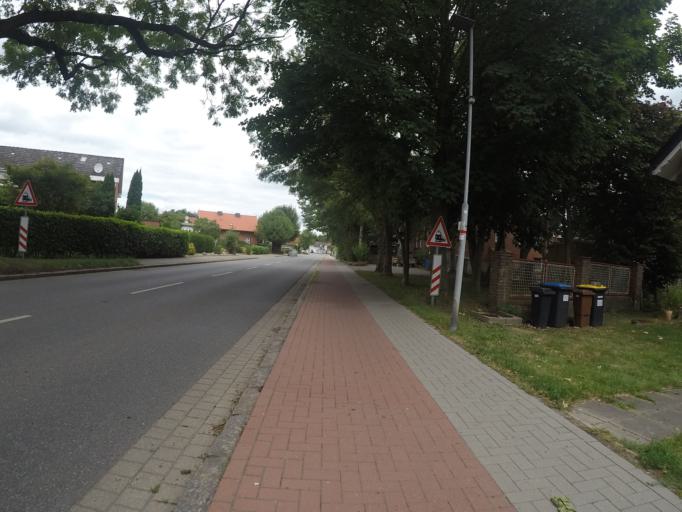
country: DE
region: Lower Saxony
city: Himmelpforten
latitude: 53.6211
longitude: 9.3079
